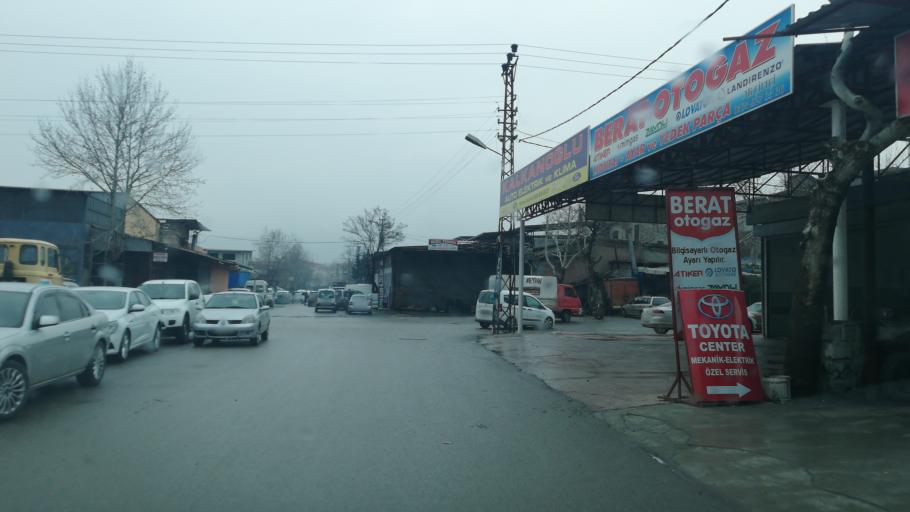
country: TR
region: Kahramanmaras
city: Kahramanmaras
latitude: 37.5649
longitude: 36.9593
